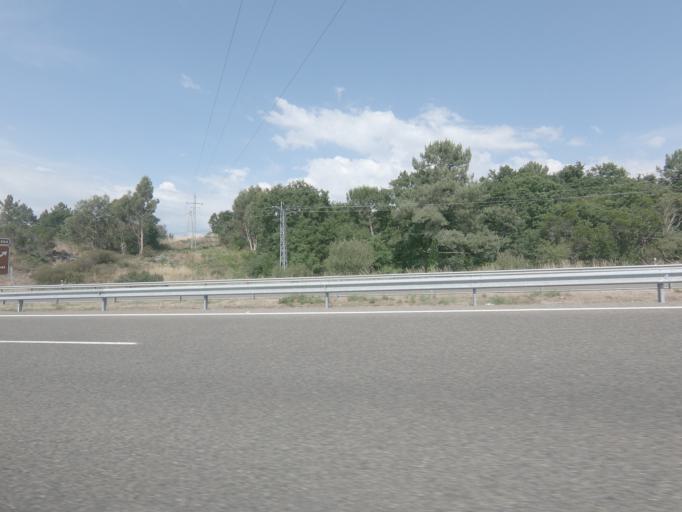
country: ES
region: Galicia
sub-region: Provincia de Ourense
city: Ourense
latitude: 42.2858
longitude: -7.8748
